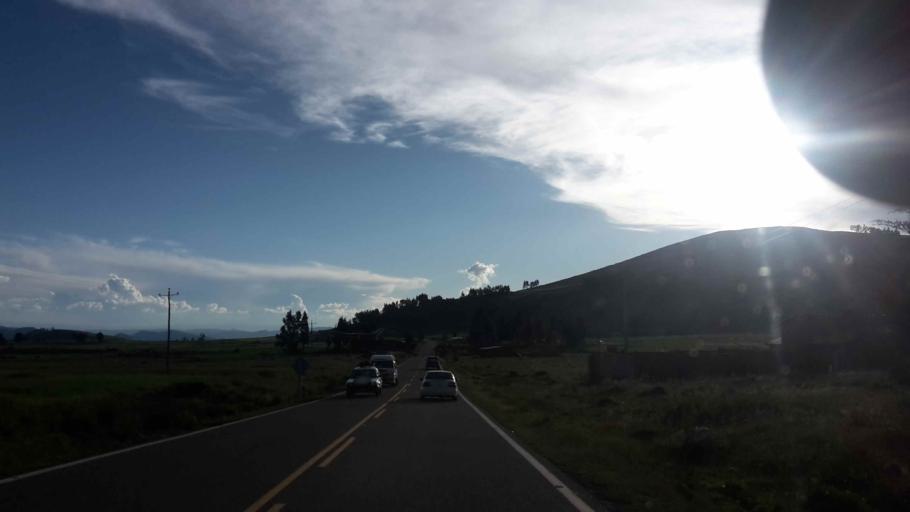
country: BO
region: Cochabamba
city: Arani
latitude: -17.5508
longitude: -65.6873
